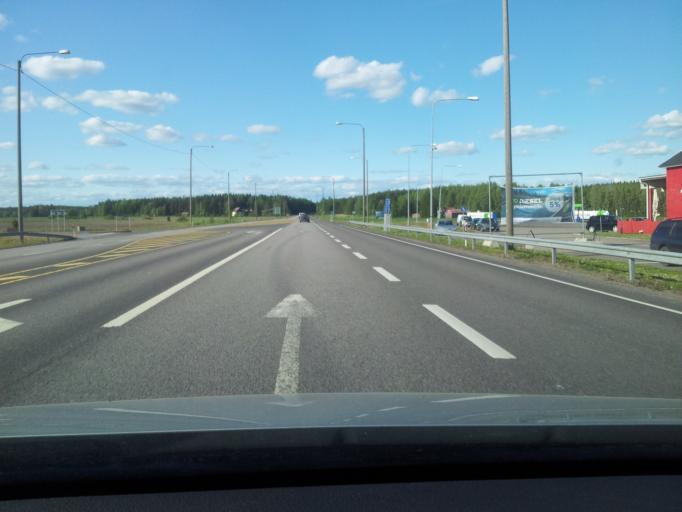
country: FI
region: Uusimaa
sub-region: Loviisa
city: Lapinjaervi
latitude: 60.6713
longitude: 26.2514
